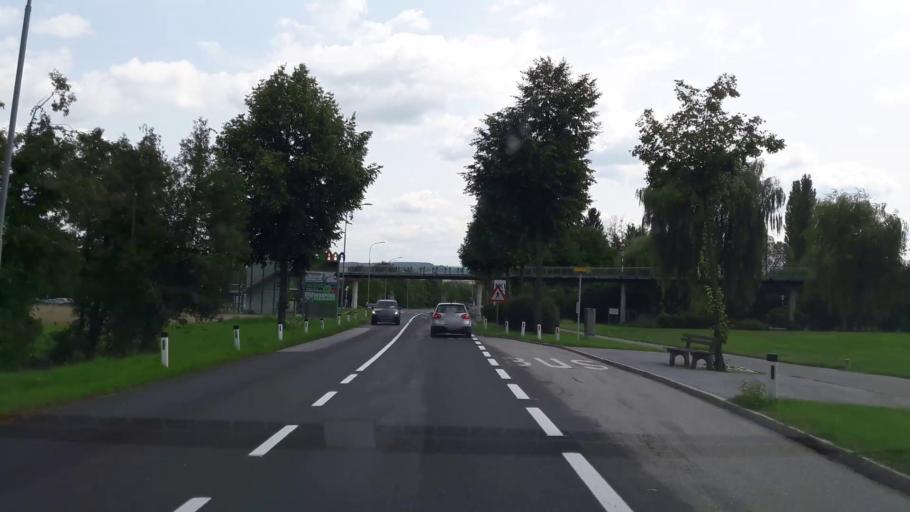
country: AT
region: Styria
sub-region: Politischer Bezirk Hartberg-Fuerstenfeld
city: Hartberg
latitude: 47.2731
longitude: 15.9677
